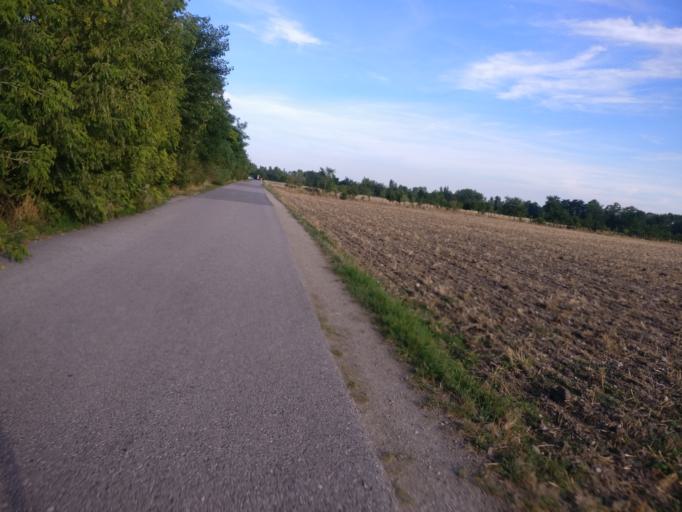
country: AT
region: Lower Austria
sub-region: Politischer Bezirk Modling
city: Biedermannsdorf
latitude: 48.0735
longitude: 16.3403
